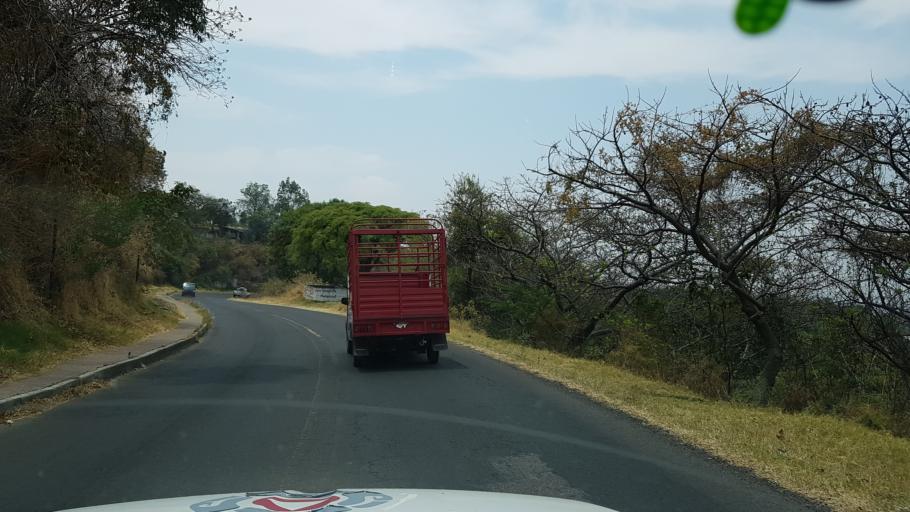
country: MX
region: Morelos
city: Ocuituco
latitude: 18.8811
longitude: -98.7774
